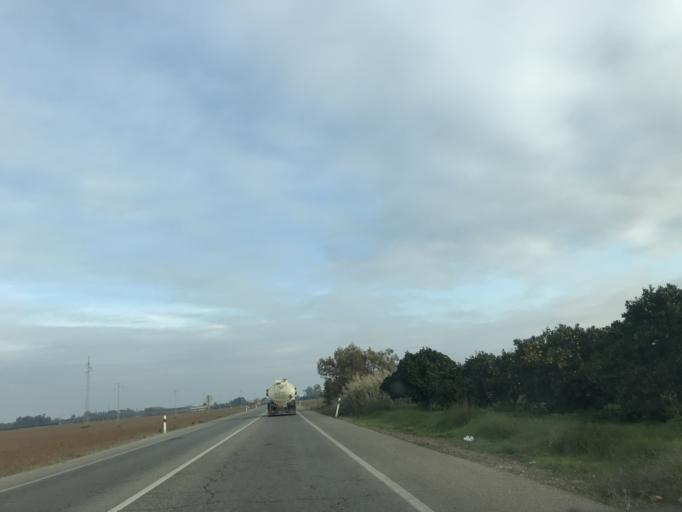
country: ES
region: Andalusia
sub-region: Provincia de Sevilla
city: La Rinconada
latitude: 37.4603
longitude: -5.9740
